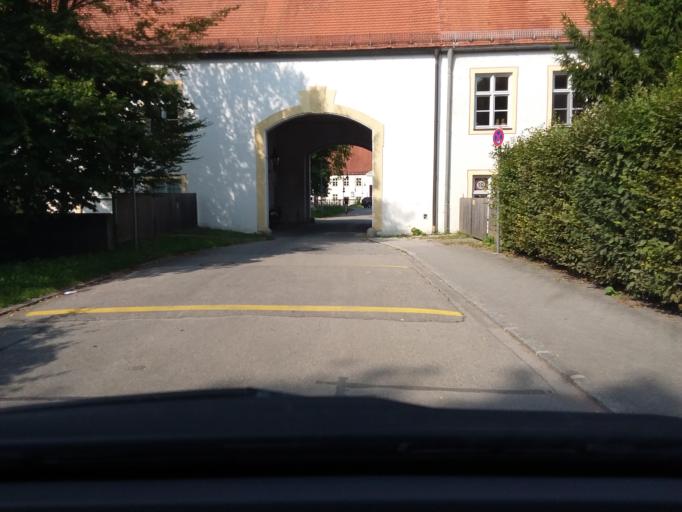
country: DE
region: Bavaria
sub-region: Upper Bavaria
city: Oberschleissheim
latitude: 48.2482
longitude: 11.5575
